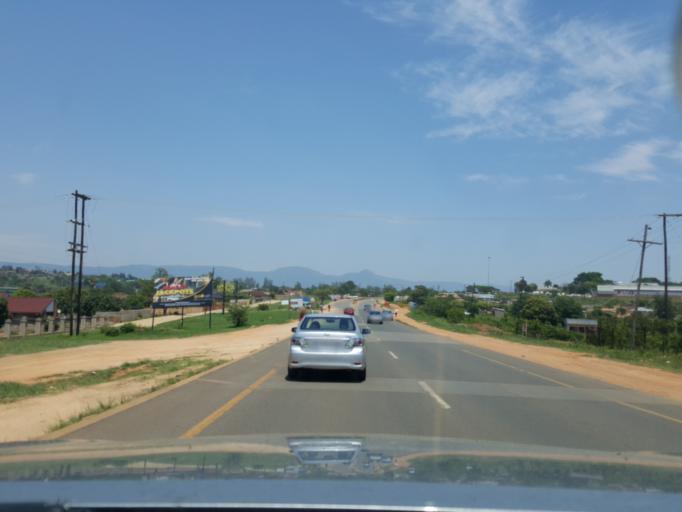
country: ZA
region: Limpopo
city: Thulamahashi
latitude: -24.8432
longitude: 31.0824
